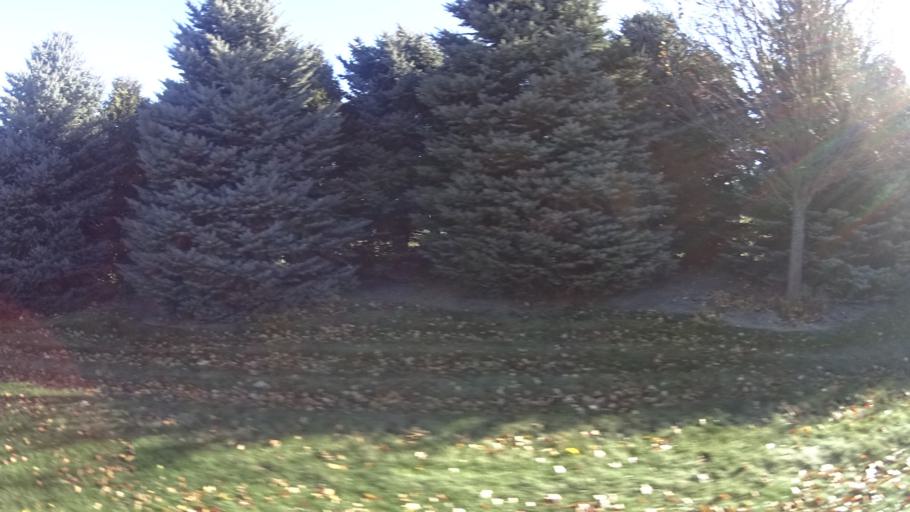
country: US
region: Ohio
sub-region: Lorain County
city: South Amherst
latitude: 41.3766
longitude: -82.2839
